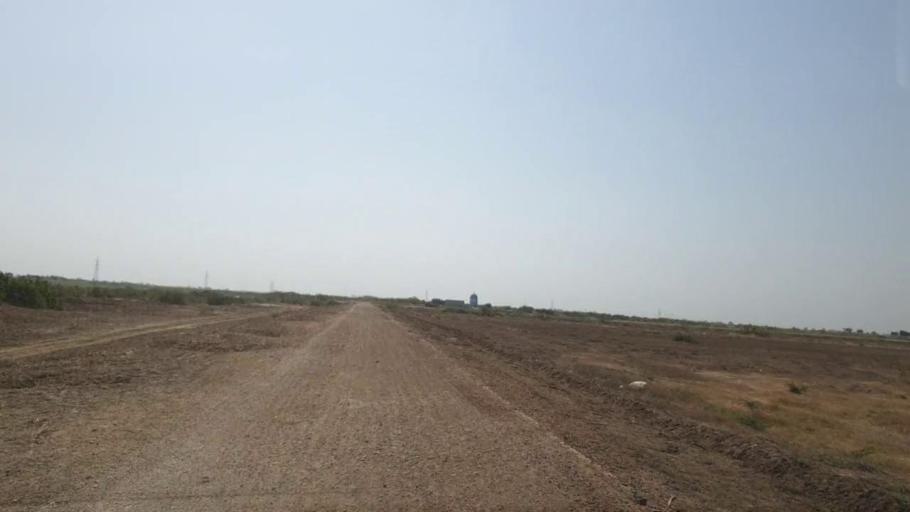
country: PK
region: Sindh
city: Naukot
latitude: 24.9737
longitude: 69.4693
